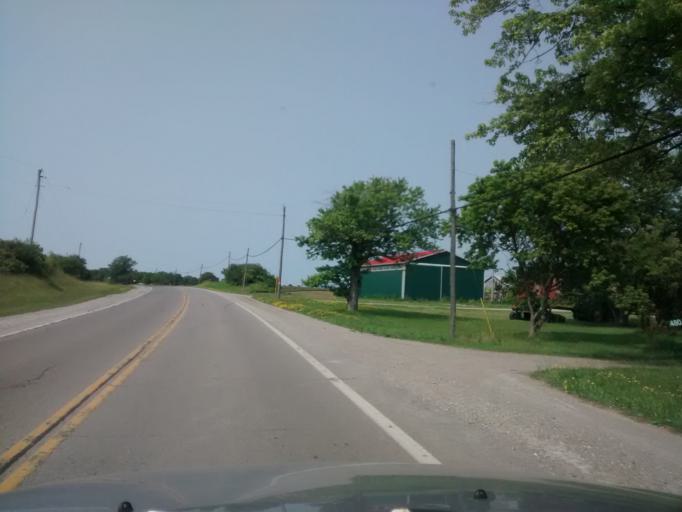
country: CA
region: Ontario
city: Ancaster
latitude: 42.9904
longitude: -79.8666
